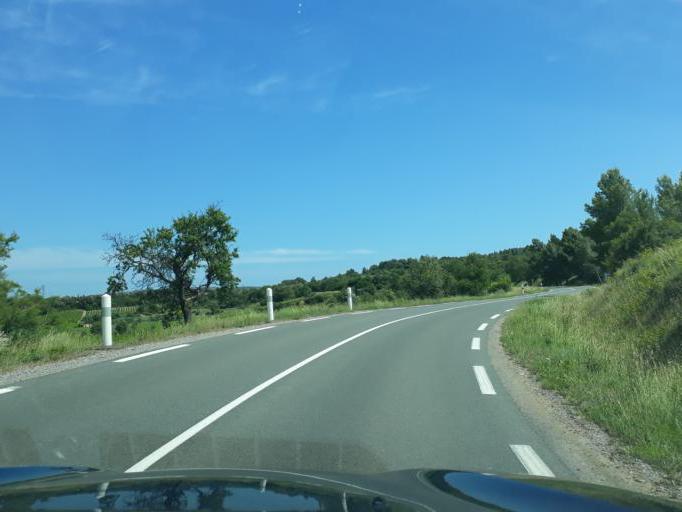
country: FR
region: Languedoc-Roussillon
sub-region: Departement de l'Aude
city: Portel-des-Corbieres
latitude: 43.0470
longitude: 2.9266
